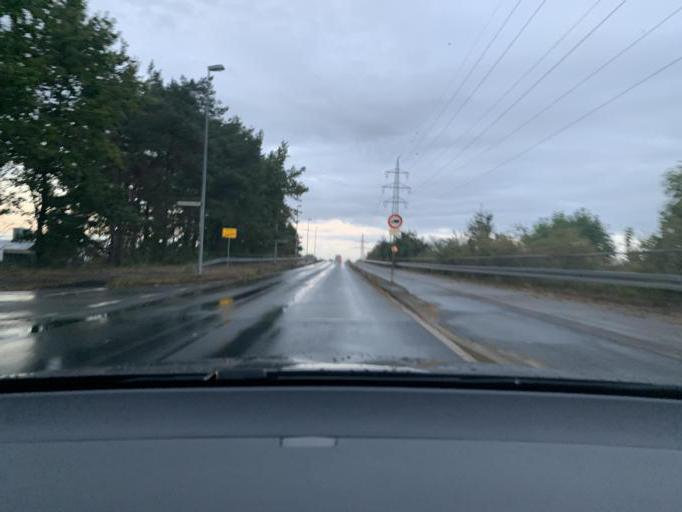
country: DE
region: Lower Saxony
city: Vordorf
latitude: 52.3168
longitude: 10.4993
